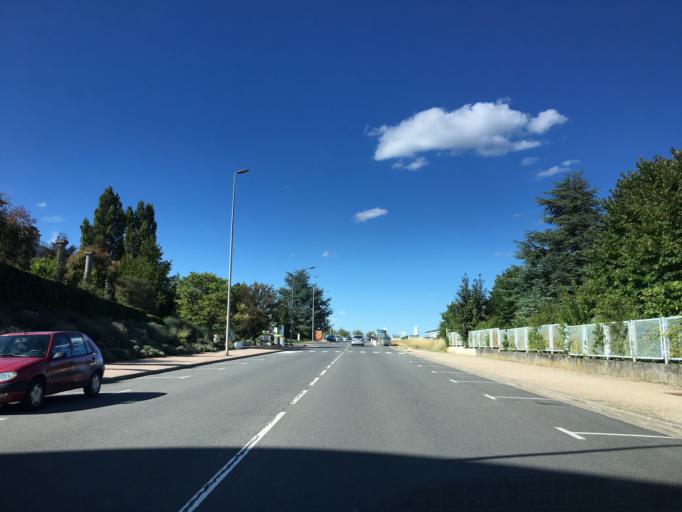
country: FR
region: Bourgogne
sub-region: Departement de l'Yonne
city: Auxerre
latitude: 47.8111
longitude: 3.5660
